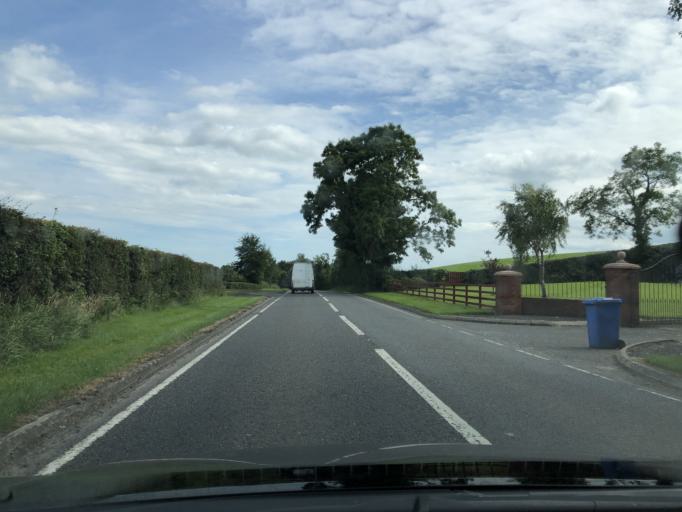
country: GB
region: Northern Ireland
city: Ballynahinch
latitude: 54.4248
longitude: -5.9221
